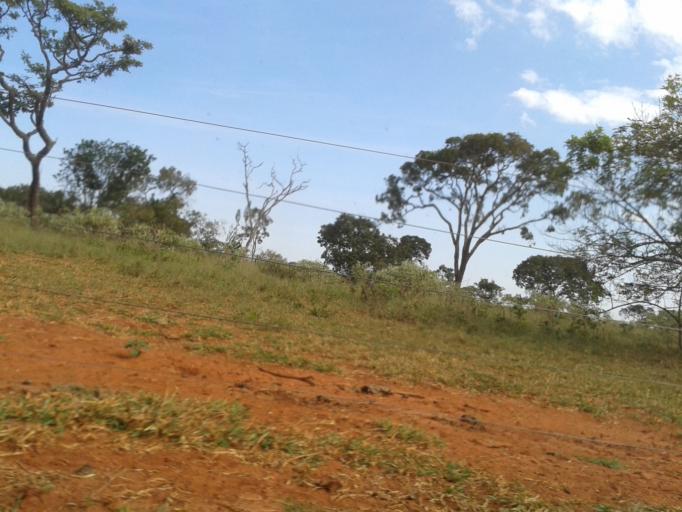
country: BR
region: Minas Gerais
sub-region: Ituiutaba
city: Ituiutaba
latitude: -19.0689
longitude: -49.3644
